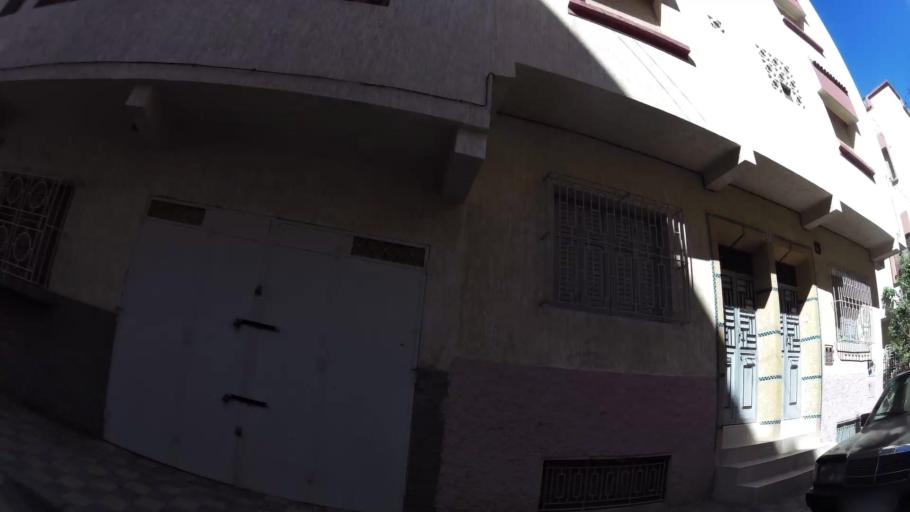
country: MA
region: Meknes-Tafilalet
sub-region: Meknes
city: Meknes
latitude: 33.8851
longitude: -5.5760
